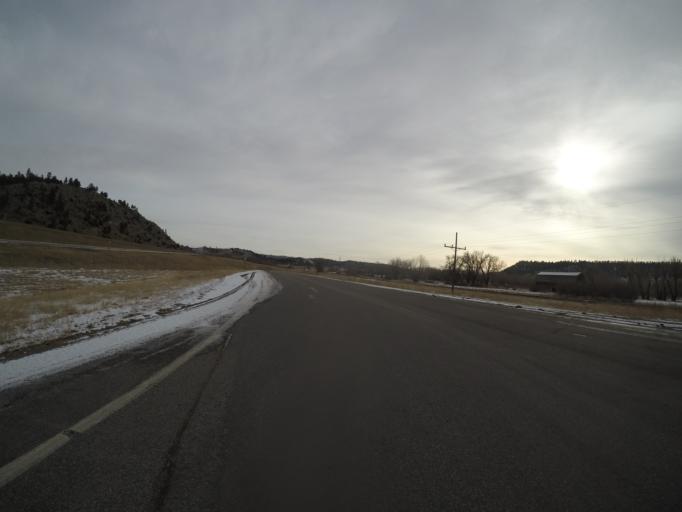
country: US
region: Montana
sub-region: Stillwater County
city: Columbus
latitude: 45.6999
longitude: -109.3887
